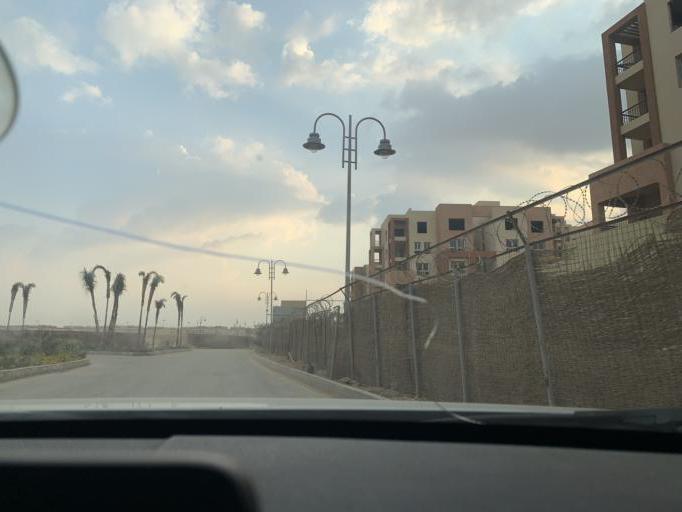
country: EG
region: Muhafazat al Qalyubiyah
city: Al Khankah
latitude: 30.0983
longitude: 31.6511
